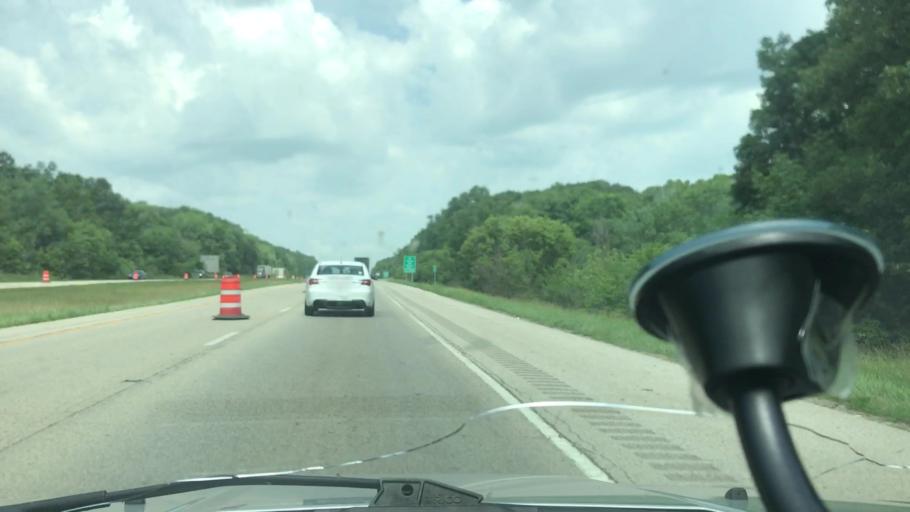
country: US
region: Illinois
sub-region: Peoria County
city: Bartonville
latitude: 40.6632
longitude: -89.6529
